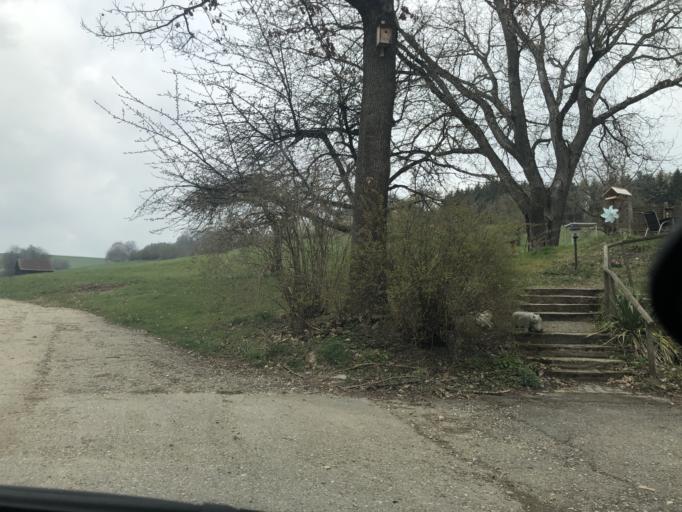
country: DE
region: Bavaria
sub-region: Upper Bavaria
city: Wolfersdorf
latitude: 48.4400
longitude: 11.7117
